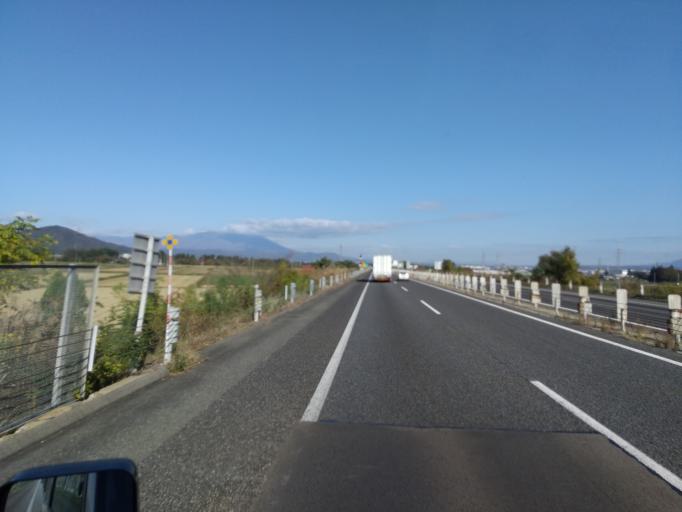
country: JP
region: Iwate
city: Morioka-shi
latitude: 39.6414
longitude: 141.1254
